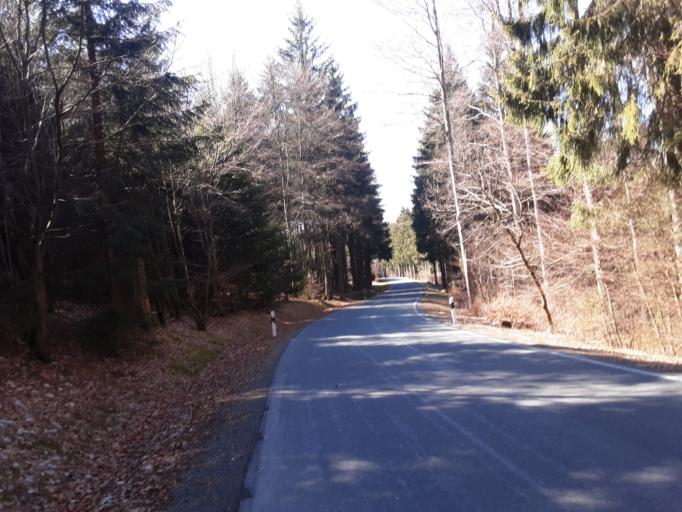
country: DE
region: North Rhine-Westphalia
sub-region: Regierungsbezirk Arnsberg
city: Winterberg
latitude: 51.2007
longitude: 8.4464
